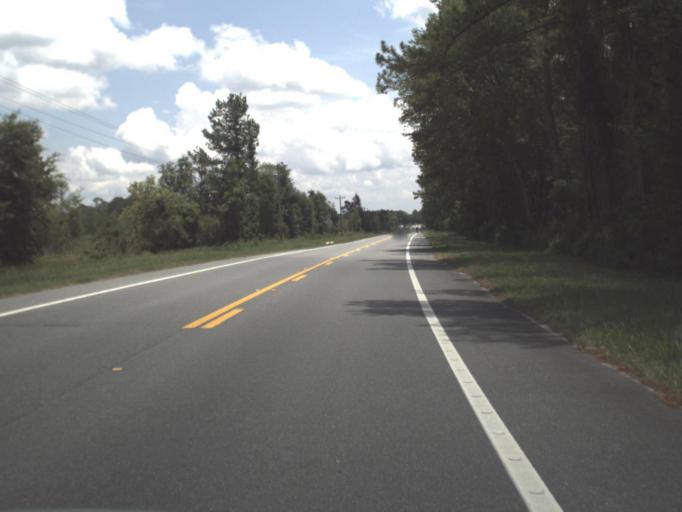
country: US
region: Florida
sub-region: Union County
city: Lake Butler
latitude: 30.0074
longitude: -82.4776
